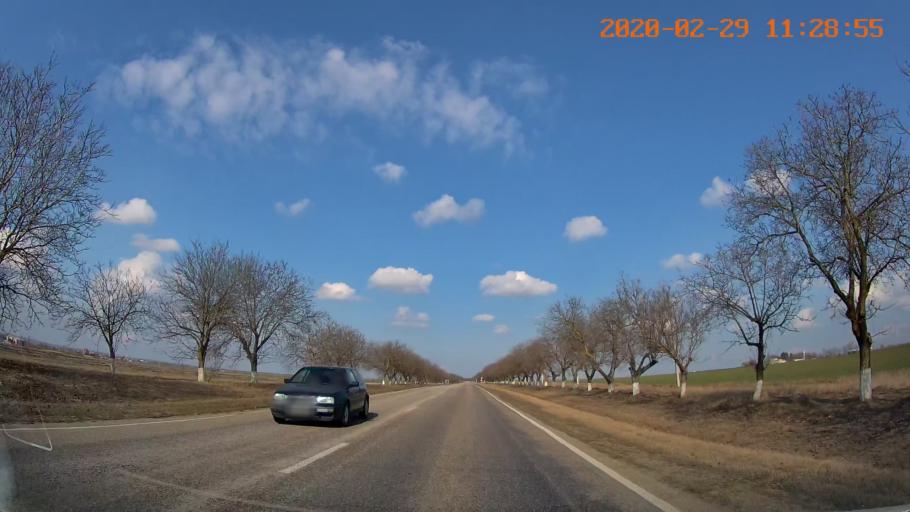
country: MD
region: Telenesti
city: Cocieri
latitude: 47.4863
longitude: 29.1300
